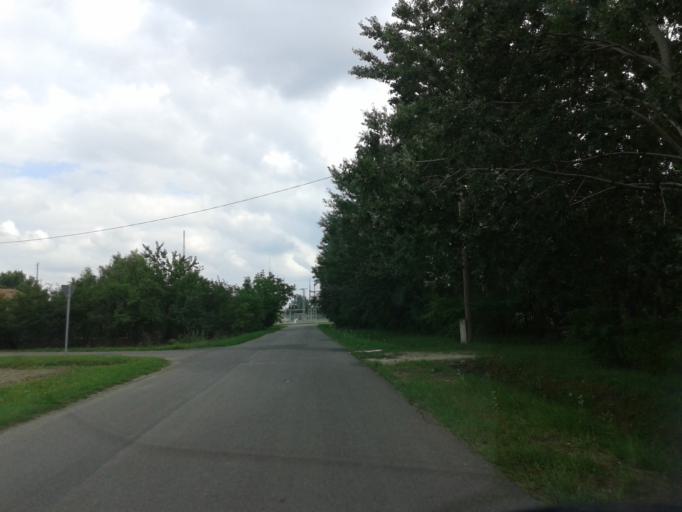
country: HU
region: Csongrad
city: Morahalom
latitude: 46.2138
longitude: 19.8948
